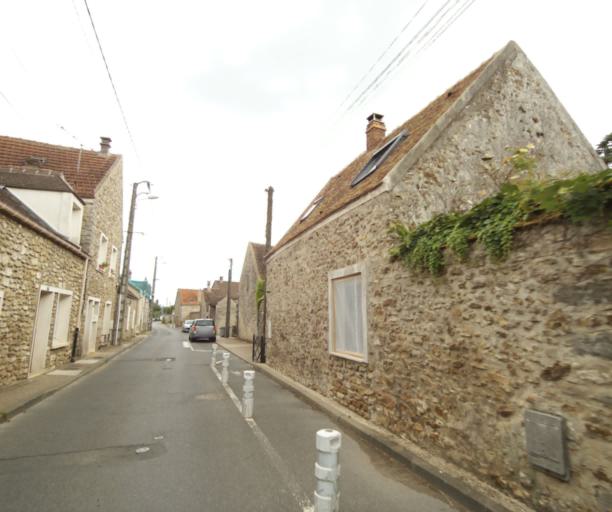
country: FR
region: Ile-de-France
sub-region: Departement de Seine-et-Marne
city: Perthes
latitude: 48.4785
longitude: 2.5513
